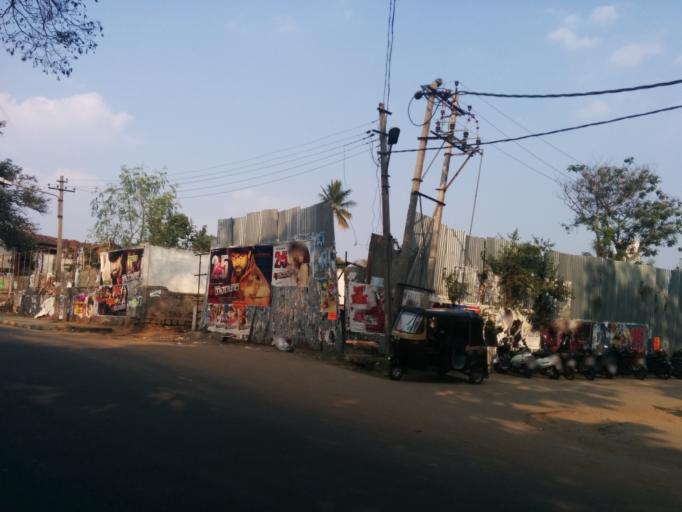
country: IN
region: Karnataka
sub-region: Mysore
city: Mysore
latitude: 12.3004
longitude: 76.6528
